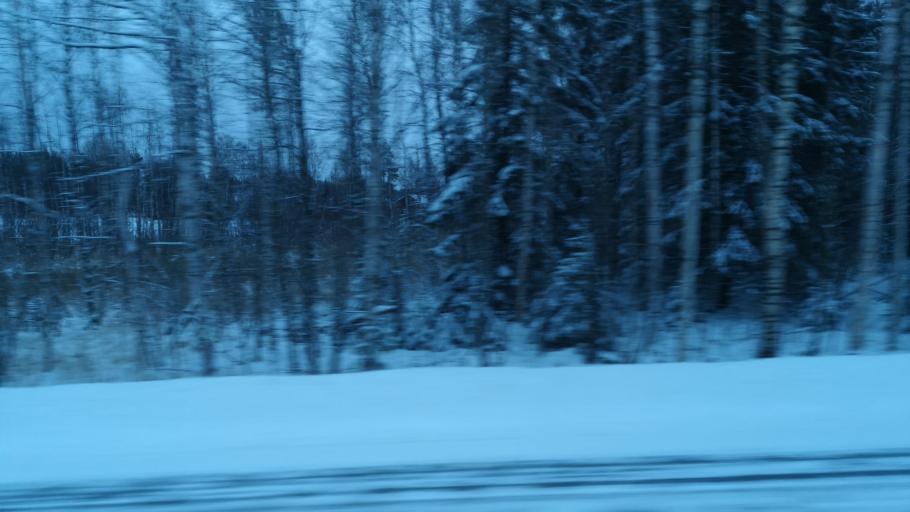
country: FI
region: Southern Savonia
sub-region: Savonlinna
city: Savonlinna
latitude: 61.8940
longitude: 28.9241
